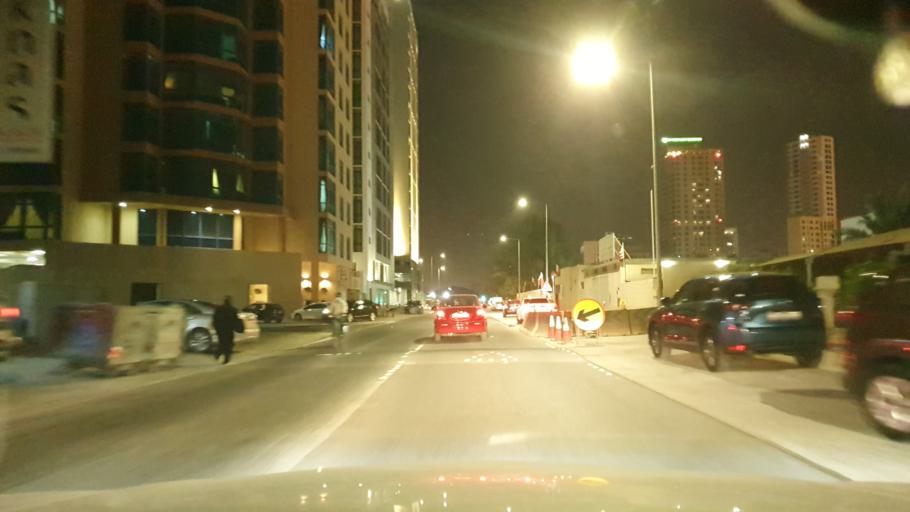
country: BH
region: Manama
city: Manama
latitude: 26.2188
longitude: 50.6010
